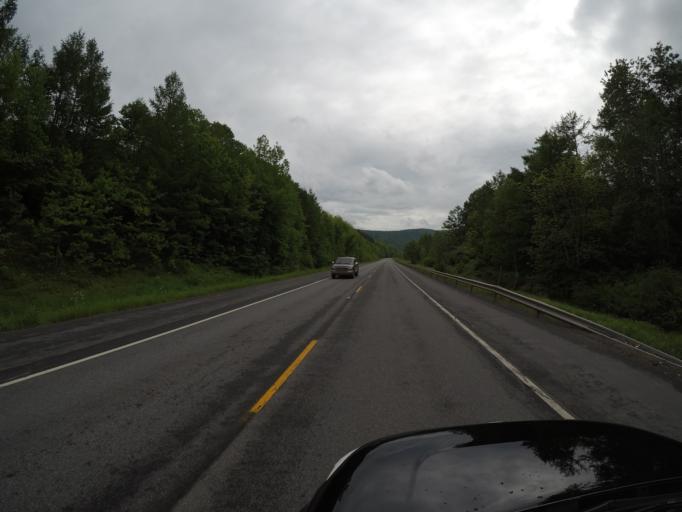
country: US
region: New York
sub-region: Delaware County
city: Stamford
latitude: 42.1336
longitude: -74.6612
